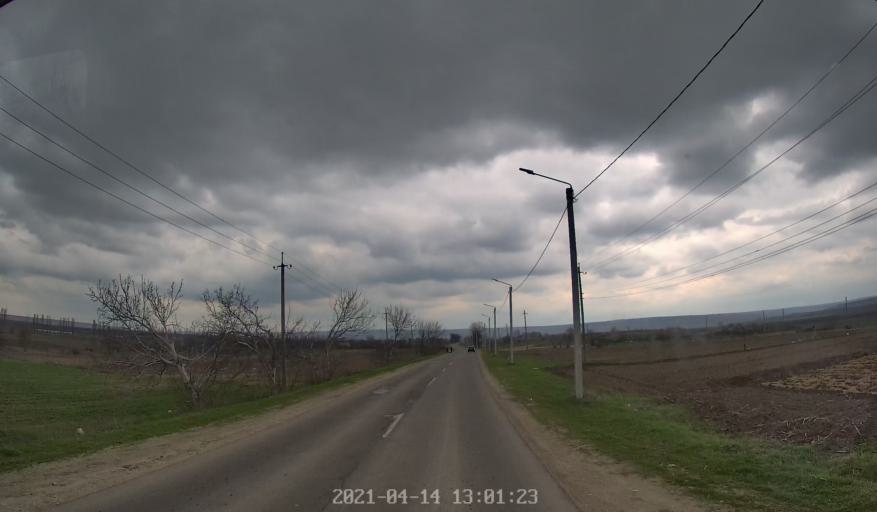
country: MD
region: Chisinau
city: Vadul lui Voda
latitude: 47.1321
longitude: 29.1167
